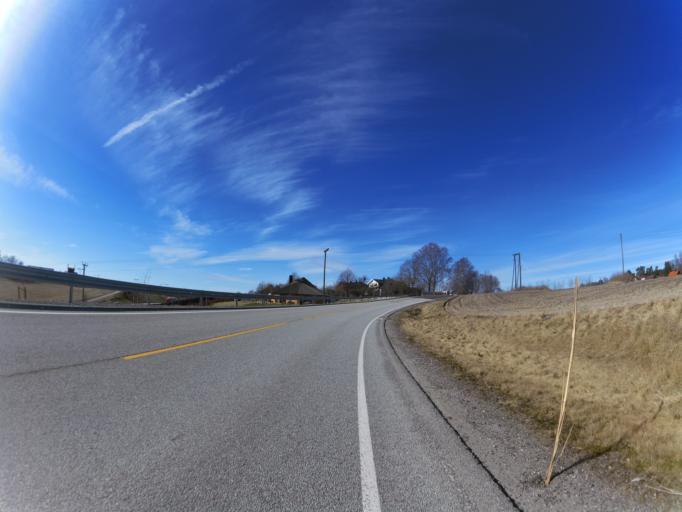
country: NO
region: Ostfold
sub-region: Fredrikstad
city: Fredrikstad
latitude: 59.3174
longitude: 10.9832
